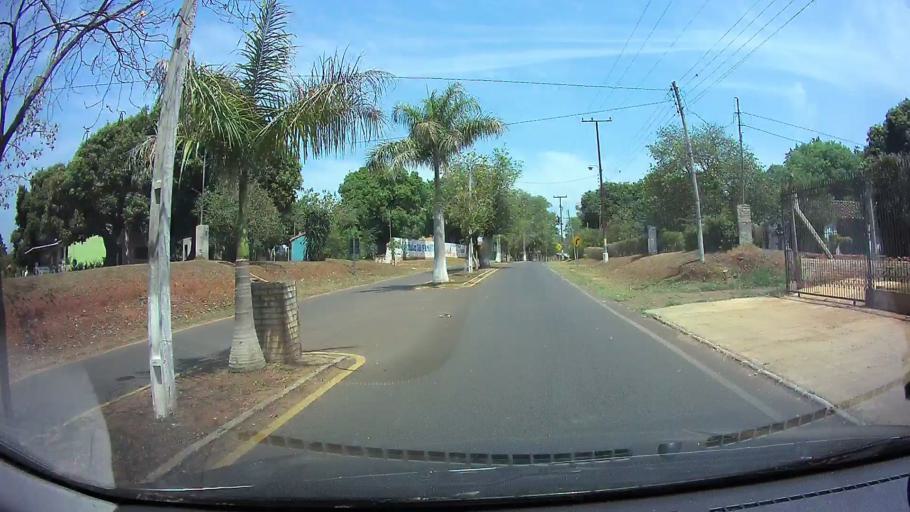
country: PY
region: Central
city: Ita
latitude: -25.4271
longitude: -57.3959
